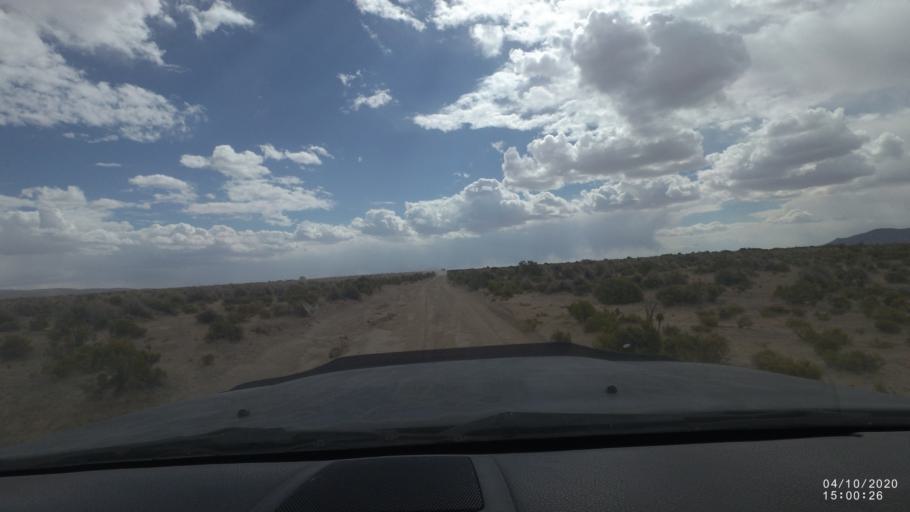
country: BO
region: Oruro
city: Poopo
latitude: -18.6865
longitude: -67.5273
